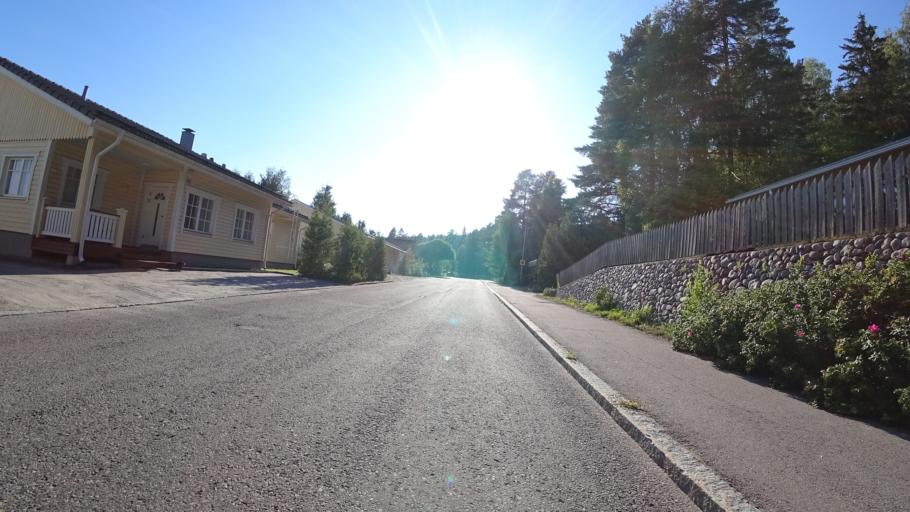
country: FI
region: Pirkanmaa
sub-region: Tampere
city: Pirkkala
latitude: 61.4995
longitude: 23.6194
